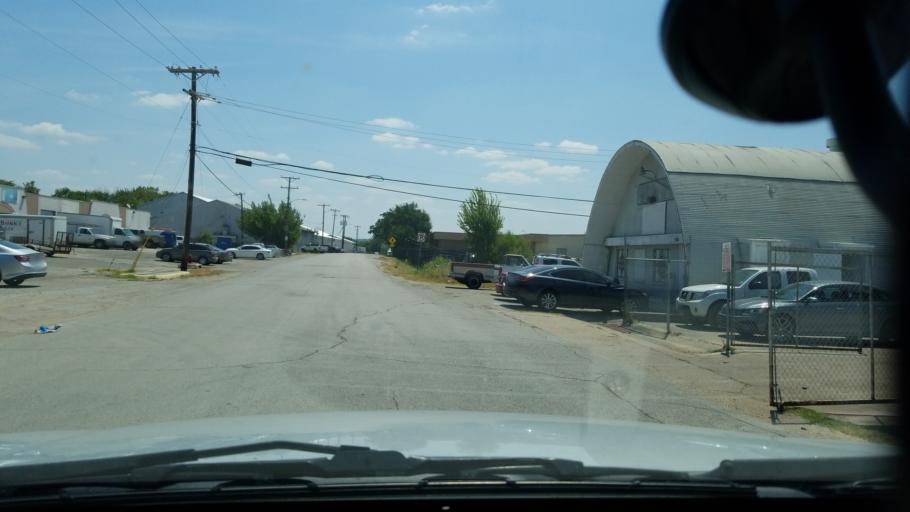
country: US
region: Texas
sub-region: Dallas County
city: Grand Prairie
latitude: 32.7494
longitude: -96.9537
